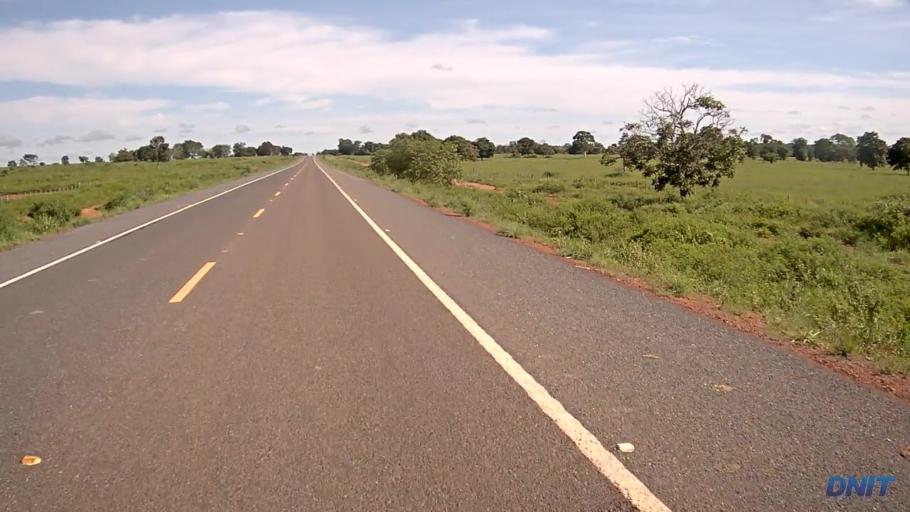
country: BR
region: Goias
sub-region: Sao Miguel Do Araguaia
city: Sao Miguel do Araguaia
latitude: -13.4764
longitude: -50.1132
